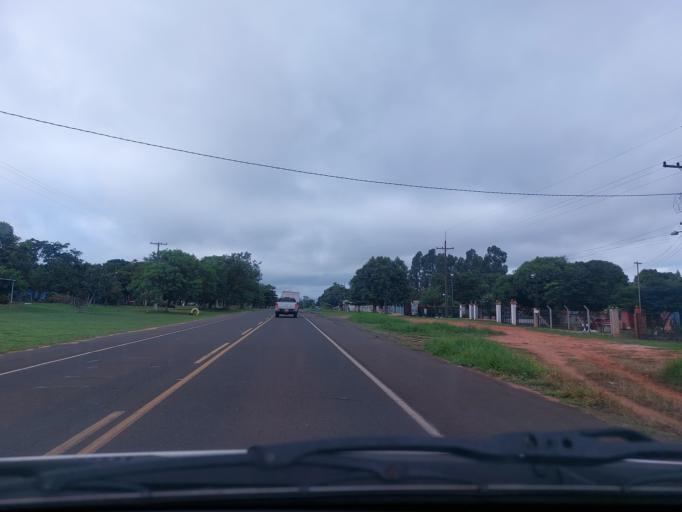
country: PY
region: San Pedro
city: Guayaybi
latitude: -24.6326
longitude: -56.3785
